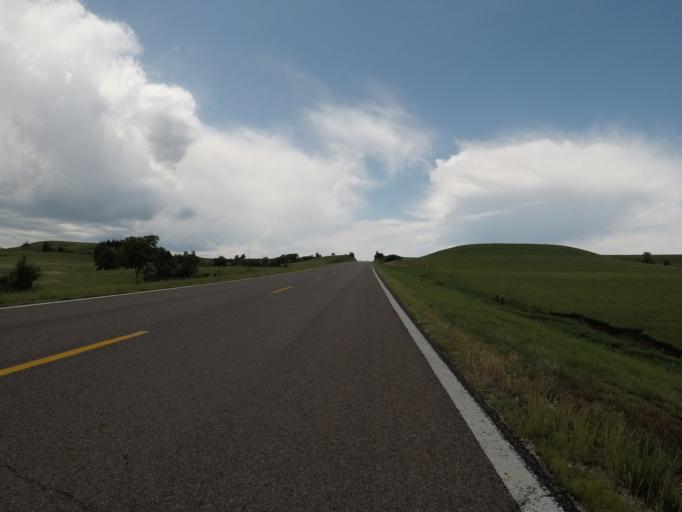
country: US
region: Kansas
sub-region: Wabaunsee County
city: Alma
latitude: 38.8711
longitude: -96.3568
